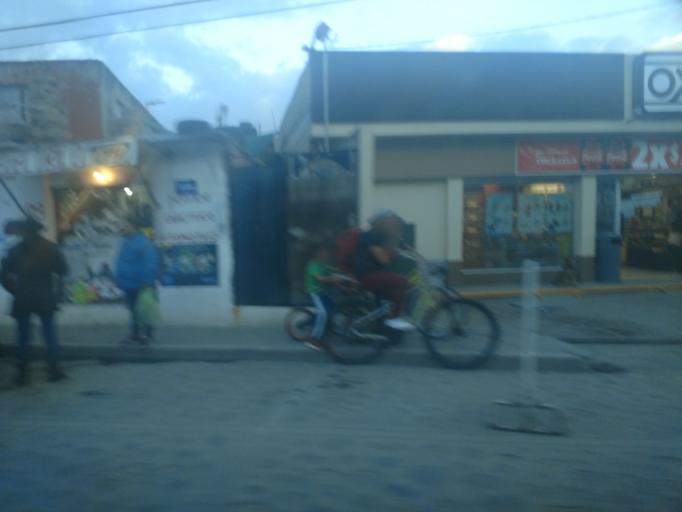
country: MX
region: Mexico
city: Tepotzotlan
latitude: 19.7187
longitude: -99.2216
